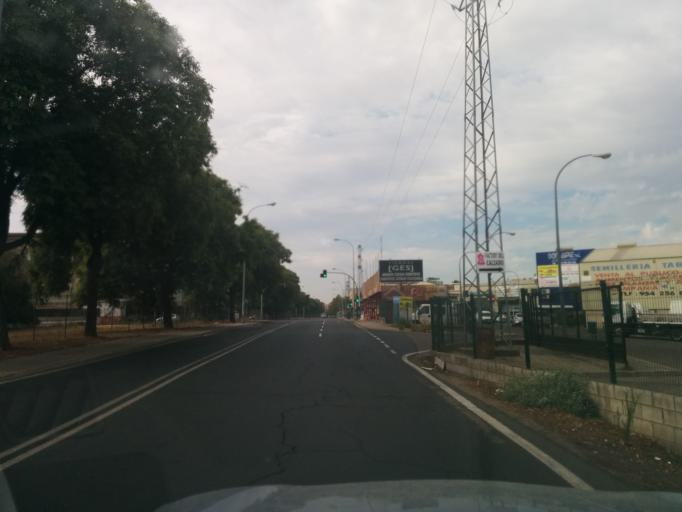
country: ES
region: Andalusia
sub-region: Provincia de Sevilla
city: Sevilla
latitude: 37.4131
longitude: -5.9315
